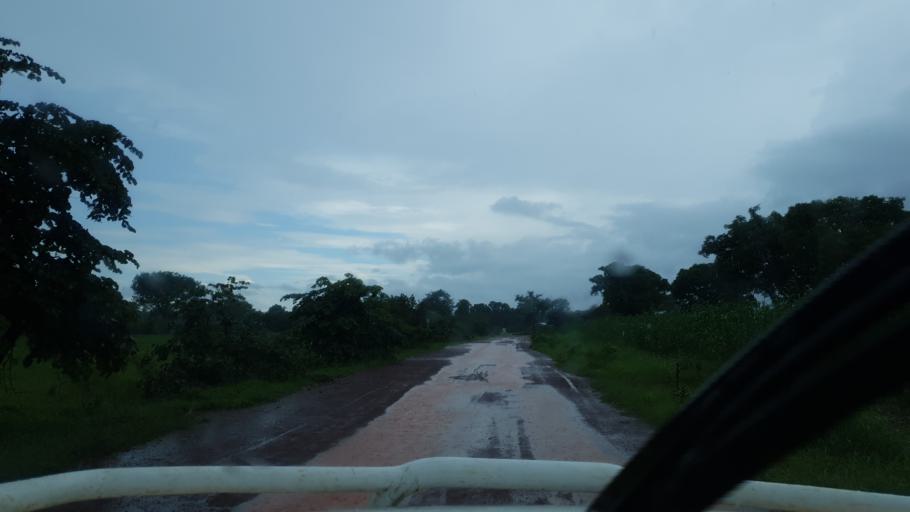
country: ML
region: Sikasso
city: Kolondieba
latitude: 11.5969
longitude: -6.6652
